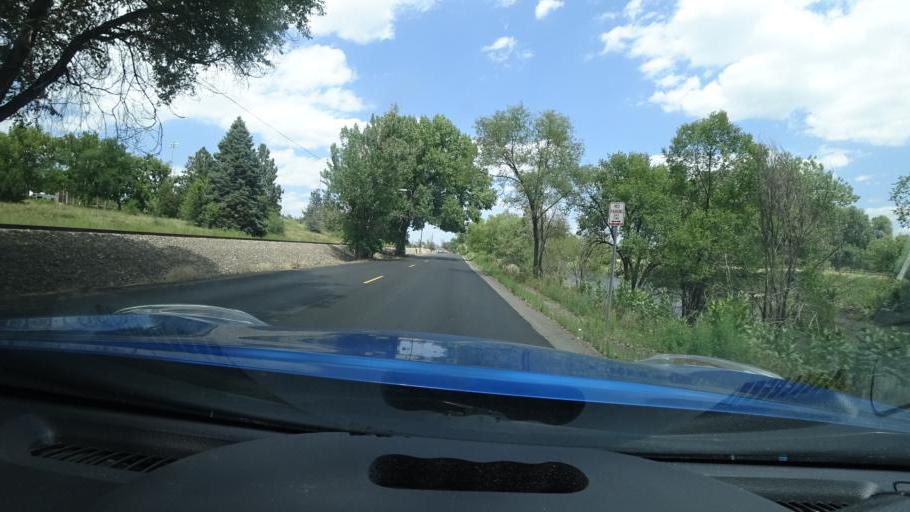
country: US
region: Colorado
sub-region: Arapahoe County
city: Englewood
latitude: 39.6832
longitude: -105.0018
